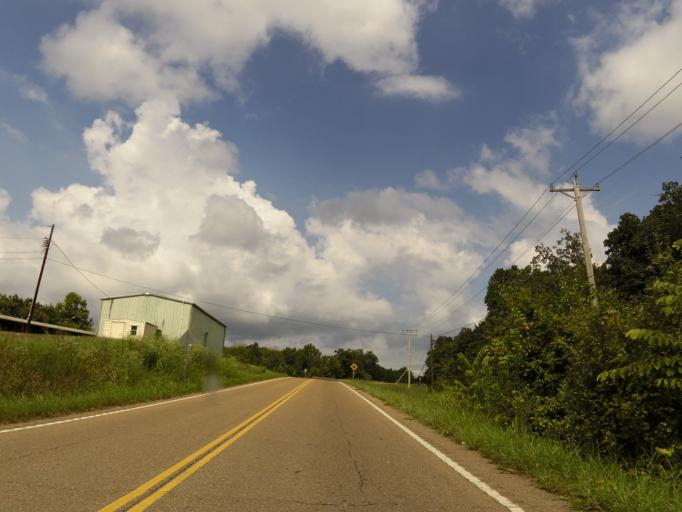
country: US
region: Tennessee
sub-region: Perry County
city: Linden
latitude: 35.6234
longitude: -87.8559
